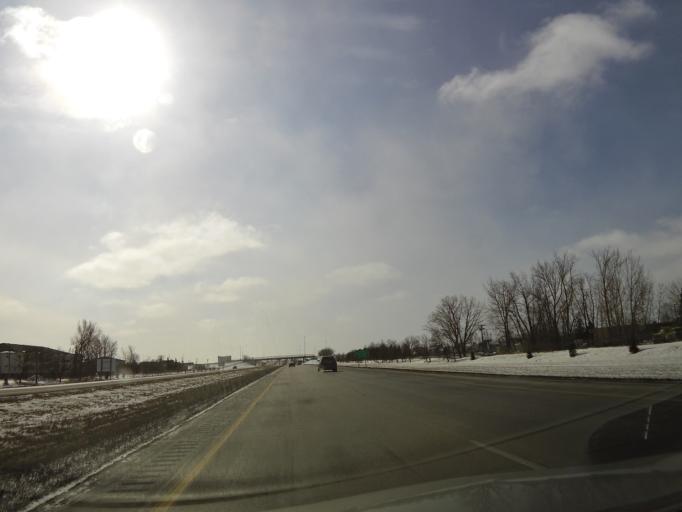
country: US
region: North Dakota
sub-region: Grand Forks County
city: Grand Forks
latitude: 47.9272
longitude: -97.0937
